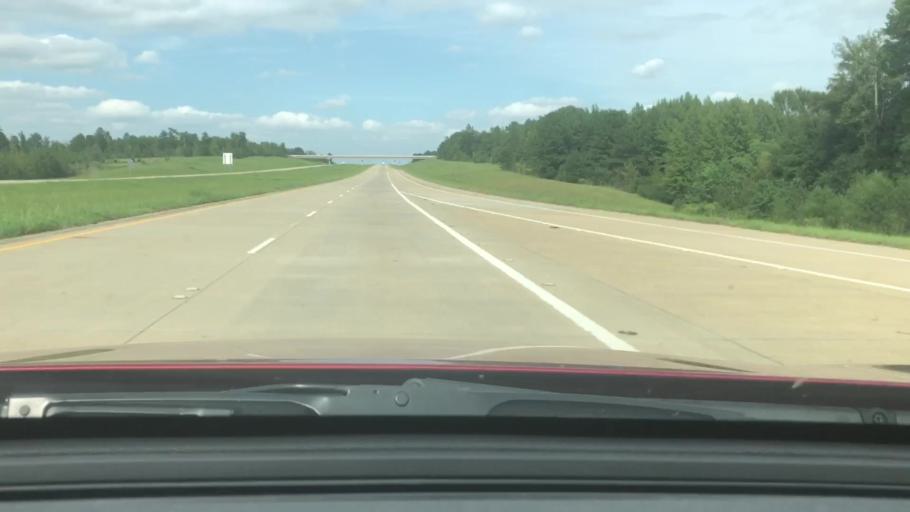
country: US
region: Louisiana
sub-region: Caddo Parish
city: Vivian
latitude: 33.0011
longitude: -93.9072
